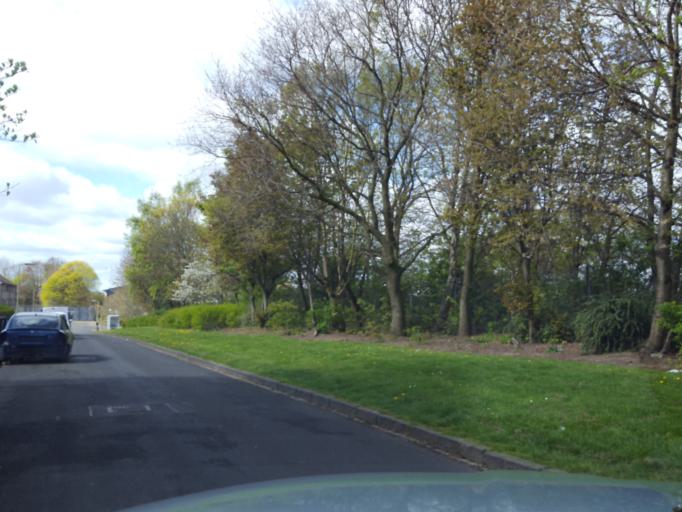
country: GB
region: Scotland
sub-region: Angus
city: Muirhead
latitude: 56.4756
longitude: -3.0420
